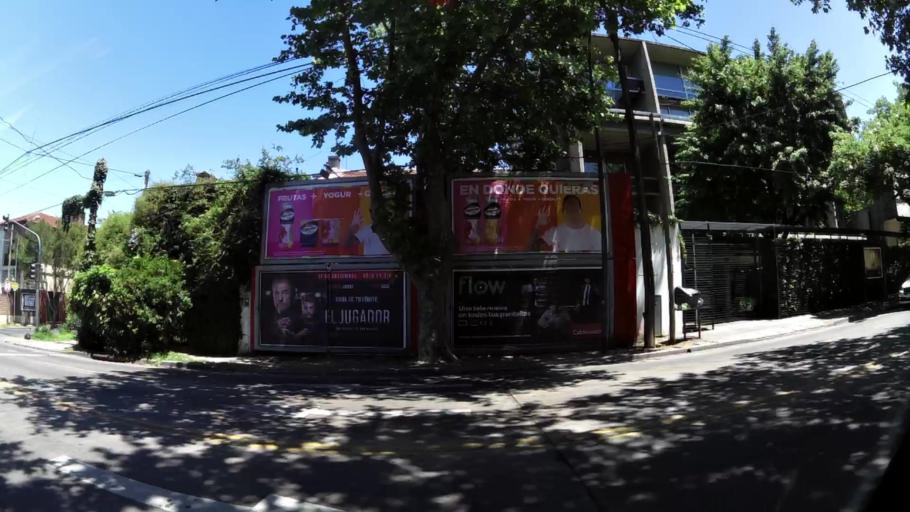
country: AR
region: Buenos Aires
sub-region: Partido de Vicente Lopez
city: Olivos
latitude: -34.5003
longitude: -58.4832
